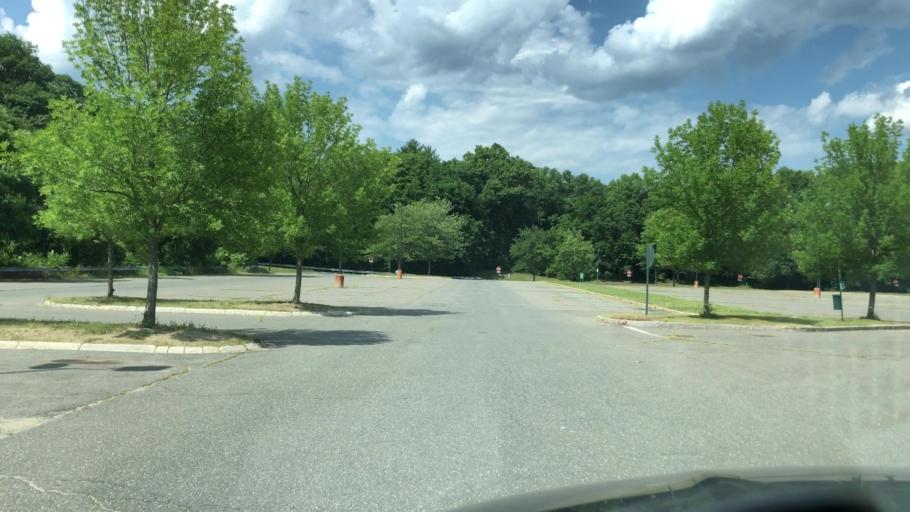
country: US
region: Massachusetts
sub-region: Hampden County
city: Holyoke
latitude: 42.1974
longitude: -72.6491
